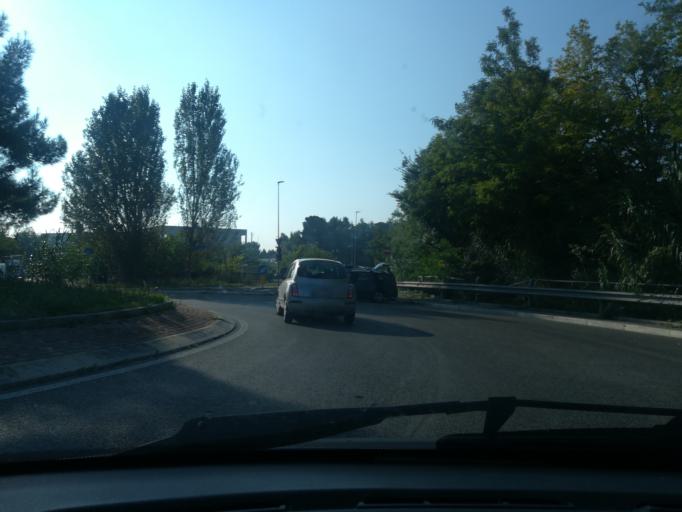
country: IT
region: The Marches
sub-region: Provincia di Macerata
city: Piediripa
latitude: 43.2886
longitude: 13.4720
